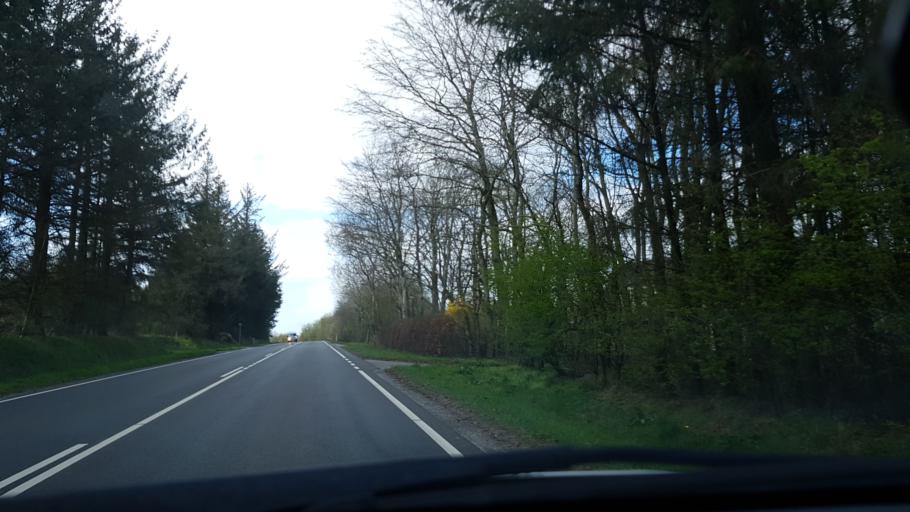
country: DK
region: South Denmark
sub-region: Esbjerg Kommune
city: Ribe
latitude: 55.2658
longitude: 8.8859
